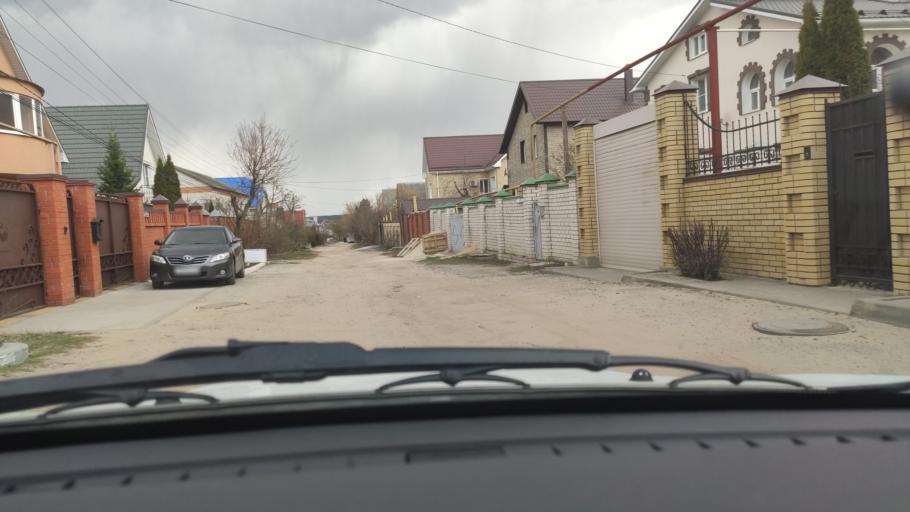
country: RU
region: Voronezj
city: Pridonskoy
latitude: 51.6586
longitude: 39.0941
